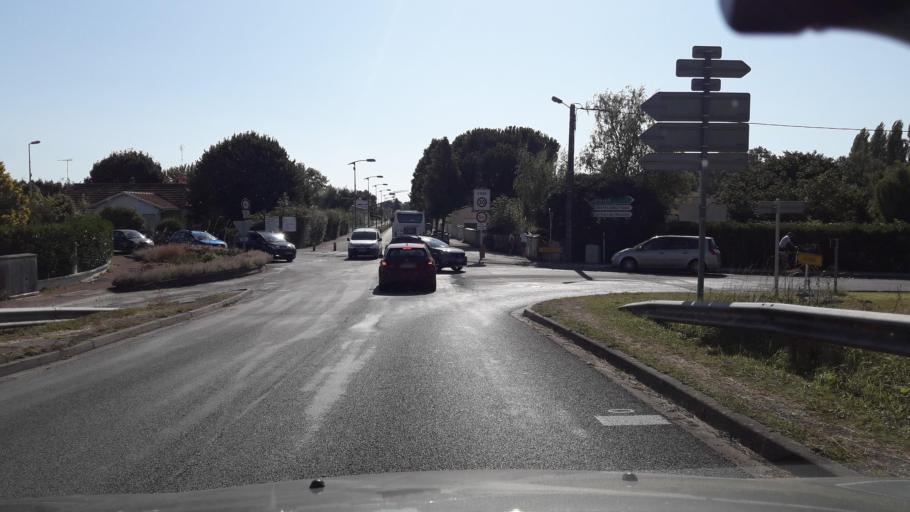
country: FR
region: Poitou-Charentes
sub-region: Departement de la Charente-Maritime
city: Saujon
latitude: 45.6724
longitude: -0.9394
